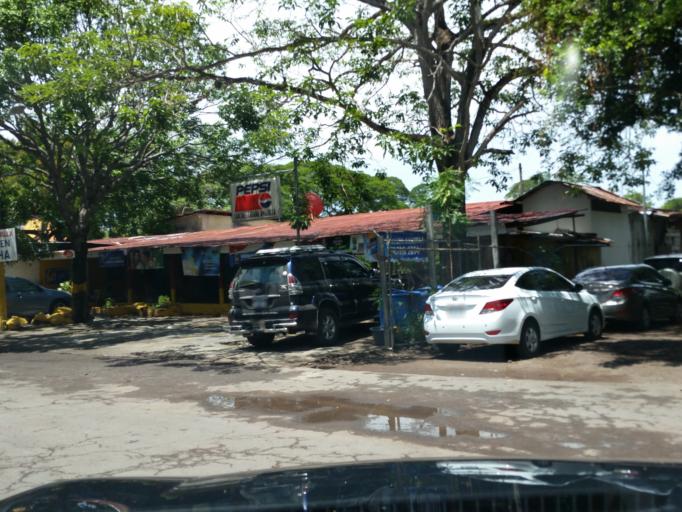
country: NI
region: Granada
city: Granada
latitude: 11.9118
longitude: -85.9298
